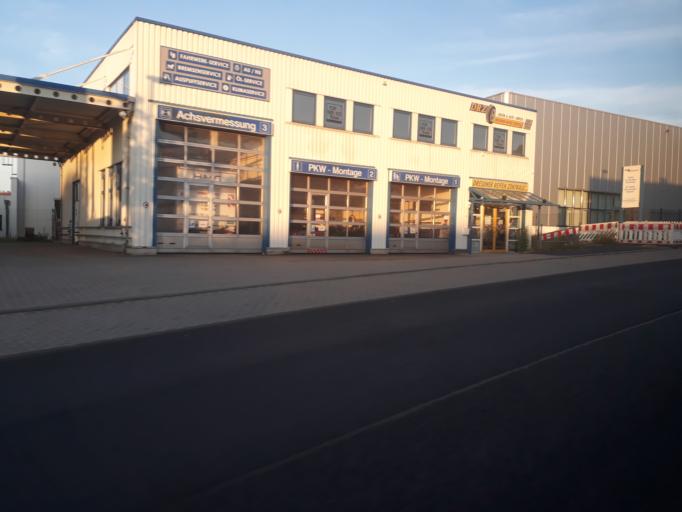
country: DE
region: Saxony
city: Radeberg
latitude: 51.0661
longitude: 13.8956
